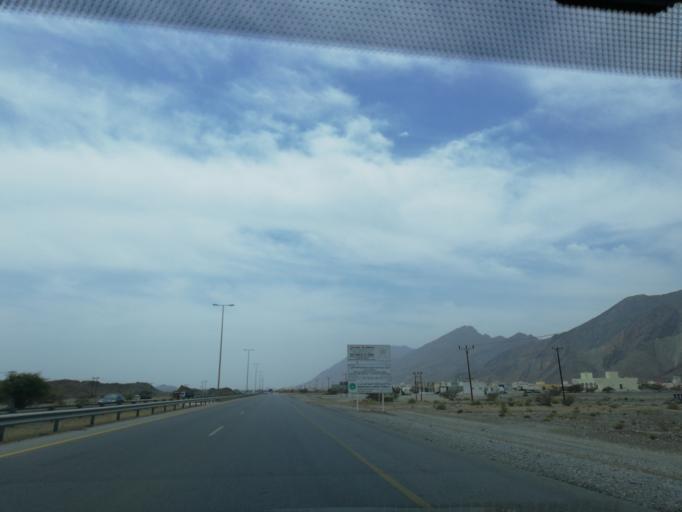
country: OM
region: Muhafazat ad Dakhiliyah
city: Izki
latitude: 23.0310
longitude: 57.7982
